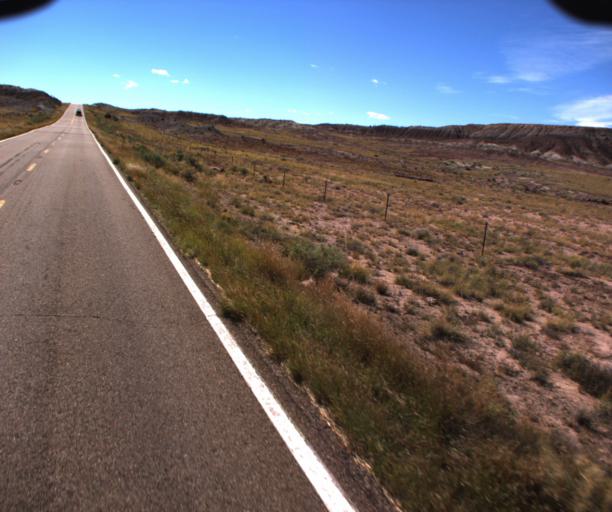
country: US
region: Arizona
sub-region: Apache County
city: Saint Johns
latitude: 34.6620
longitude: -109.2929
